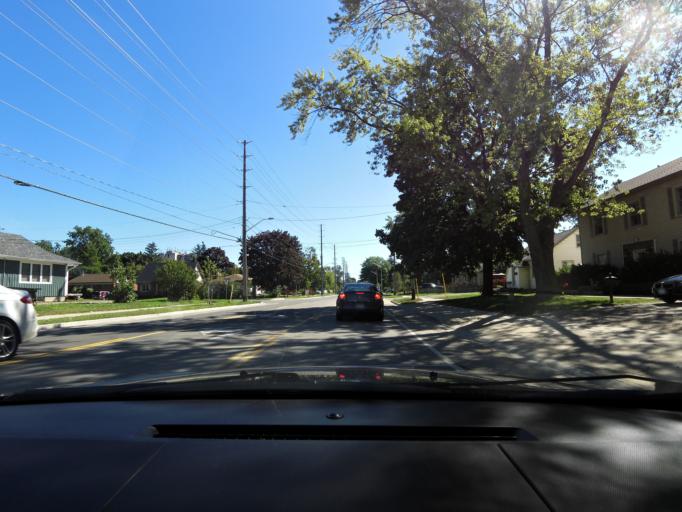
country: CA
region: Ontario
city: Burlington
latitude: 43.3237
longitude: -79.8354
